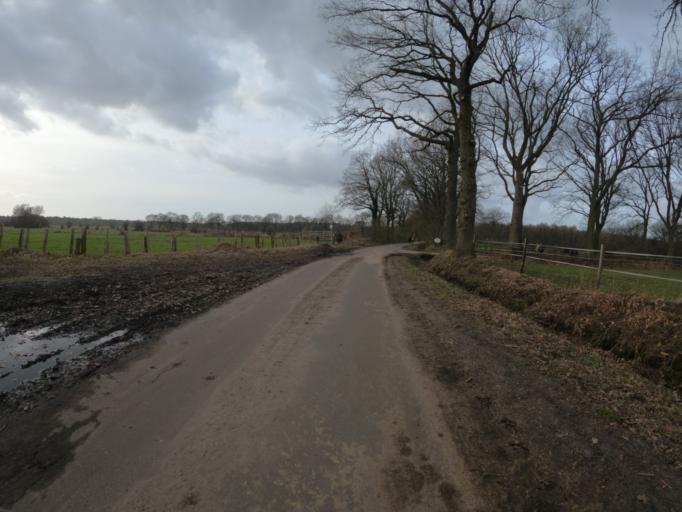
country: DE
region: Schleswig-Holstein
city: Rellingen
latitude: 53.6011
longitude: 9.7915
